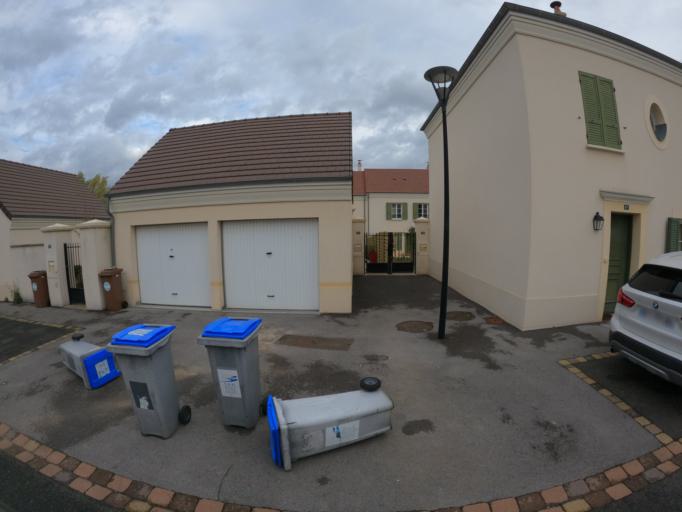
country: FR
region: Ile-de-France
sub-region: Departement de Seine-et-Marne
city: Magny-le-Hongre
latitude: 48.8721
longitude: 2.8165
